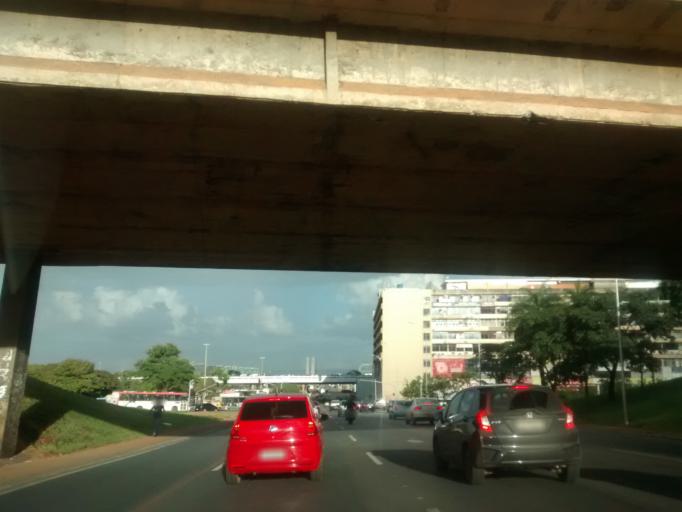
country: BR
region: Federal District
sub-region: Brasilia
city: Brasilia
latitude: -15.7940
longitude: -47.8861
